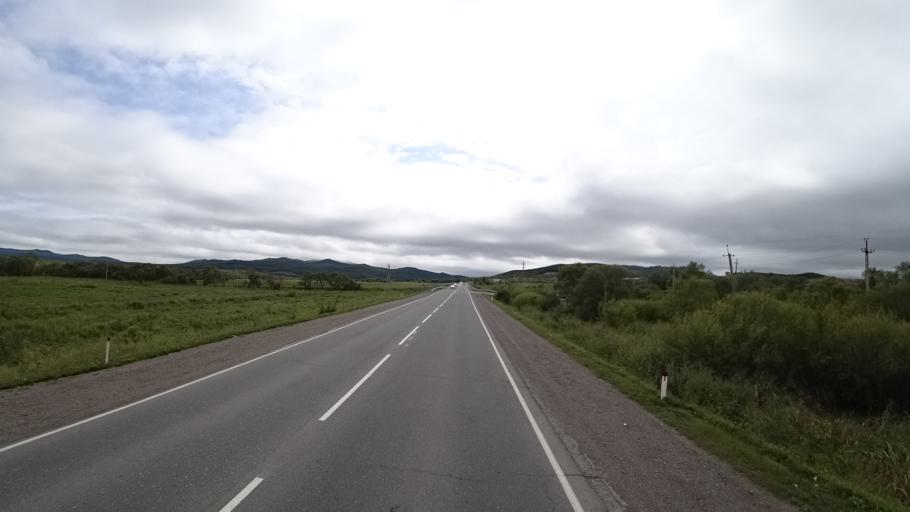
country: RU
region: Primorskiy
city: Monastyrishche
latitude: 44.1772
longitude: 132.4415
